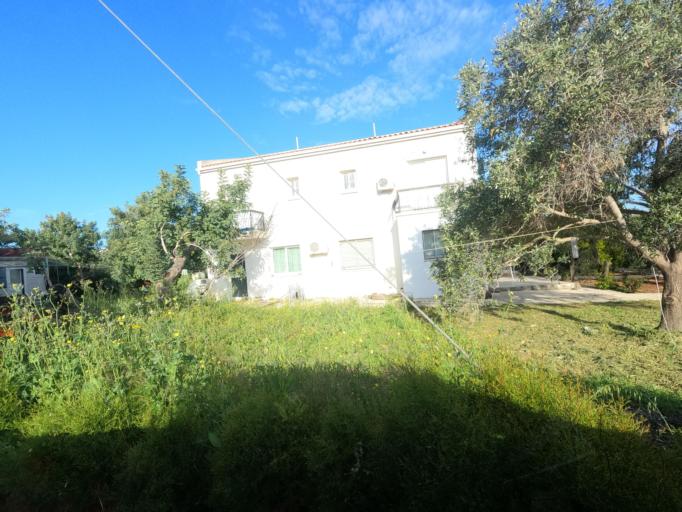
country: CY
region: Pafos
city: Polis
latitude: 35.0384
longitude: 32.3841
